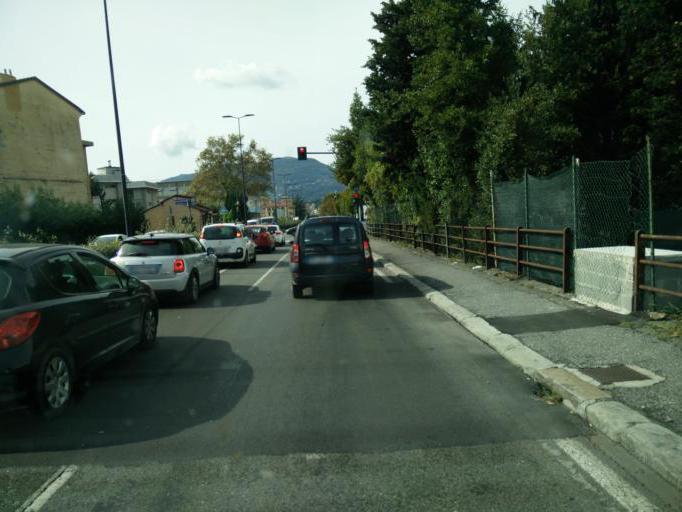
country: IT
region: Liguria
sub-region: Provincia di La Spezia
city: La Spezia
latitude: 44.1137
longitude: 9.8493
